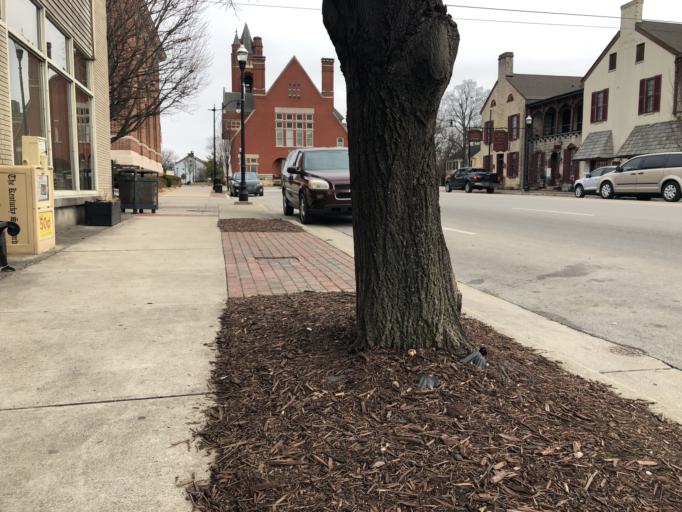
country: US
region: Kentucky
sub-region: Nelson County
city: Bardstown
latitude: 37.8094
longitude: -85.4678
